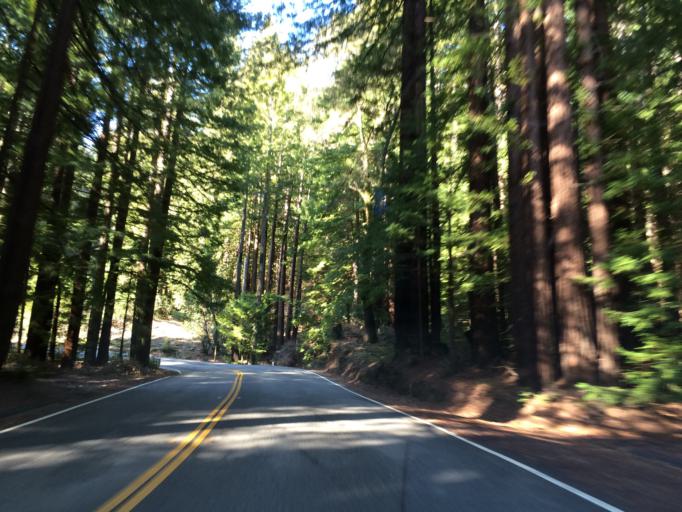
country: US
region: California
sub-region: Santa Cruz County
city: Boulder Creek
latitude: 37.2144
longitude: -122.1477
